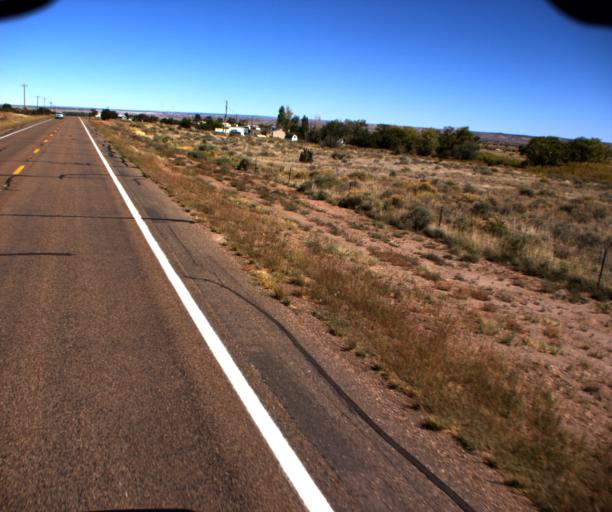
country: US
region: Arizona
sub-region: Apache County
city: Saint Johns
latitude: 34.4663
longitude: -109.3961
